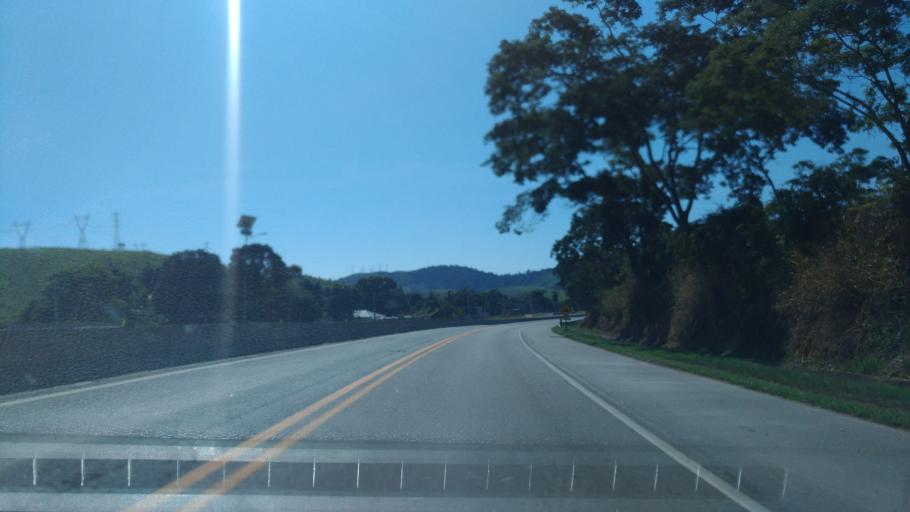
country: BR
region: Rio de Janeiro
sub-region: Macae
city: Macae
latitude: -22.0257
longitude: -41.6915
